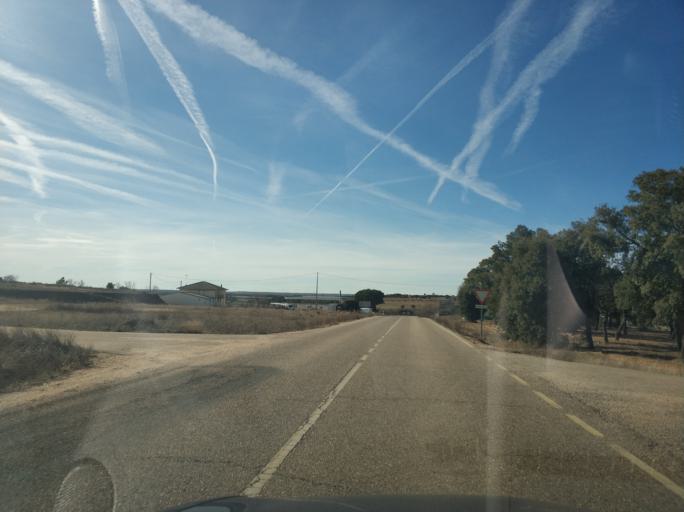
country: ES
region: Castille and Leon
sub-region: Provincia de Zamora
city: Cuelgamures
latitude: 41.2627
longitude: -5.7105
